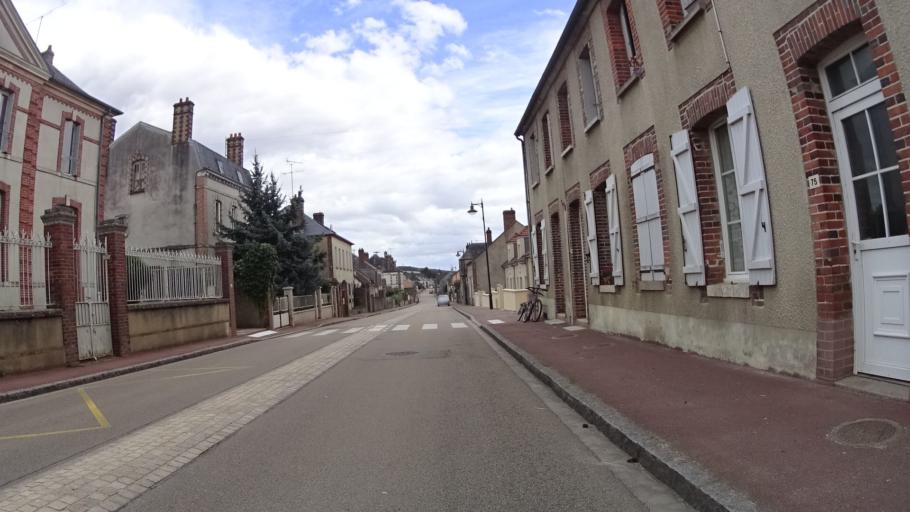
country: FR
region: Centre
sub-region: Departement du Loiret
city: Douchy
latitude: 47.9437
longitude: 3.0487
